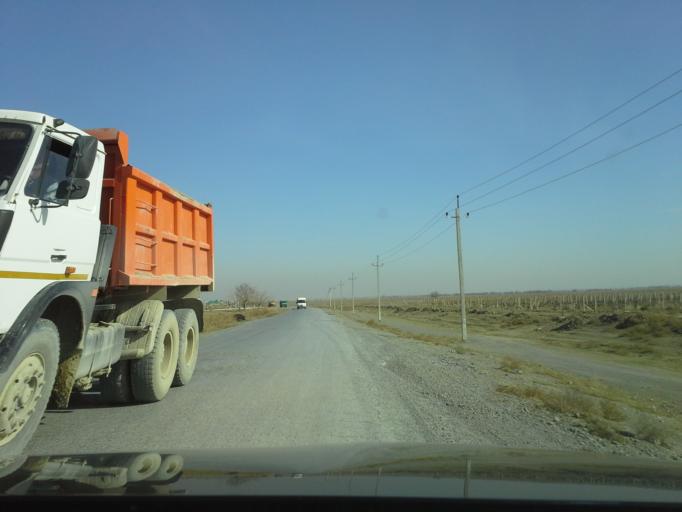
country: TM
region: Ahal
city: Abadan
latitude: 38.1105
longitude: 57.9864
